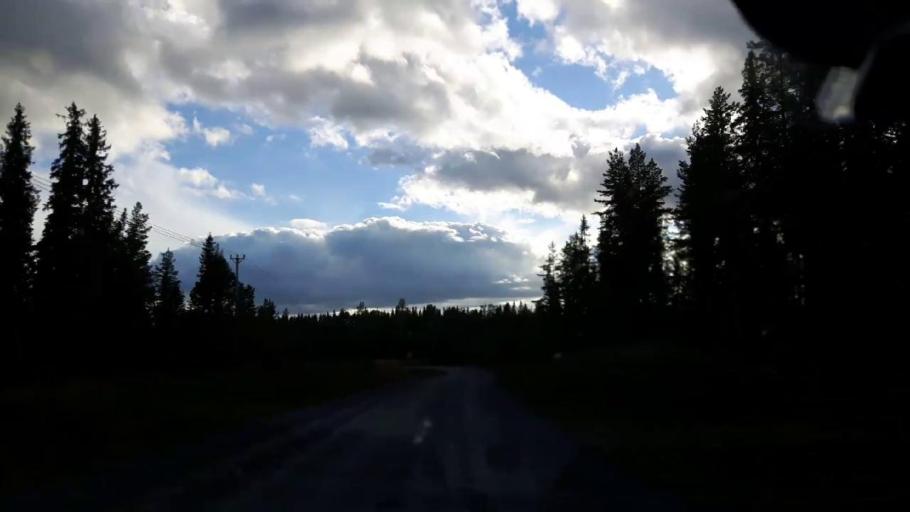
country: SE
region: Jaemtland
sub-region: Stroemsunds Kommun
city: Stroemsund
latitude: 63.3334
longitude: 15.5759
